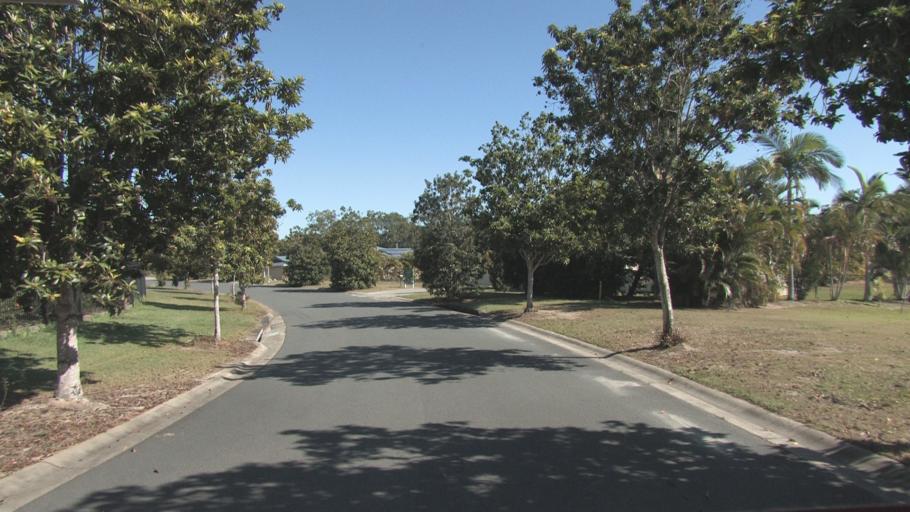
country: AU
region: Queensland
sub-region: Logan
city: Park Ridge South
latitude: -27.6864
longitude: 153.0082
